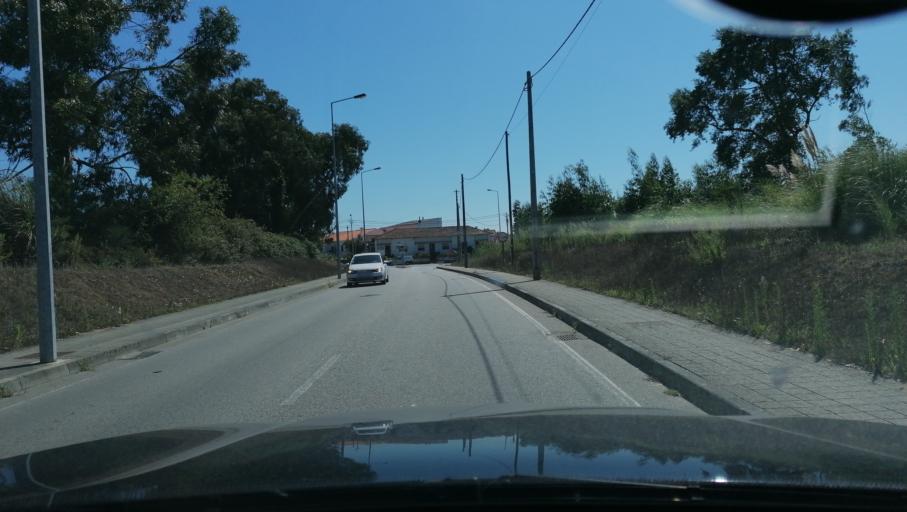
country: PT
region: Porto
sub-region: Vila Nova de Gaia
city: Vila Nova da Telha
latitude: 41.0748
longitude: -8.6432
